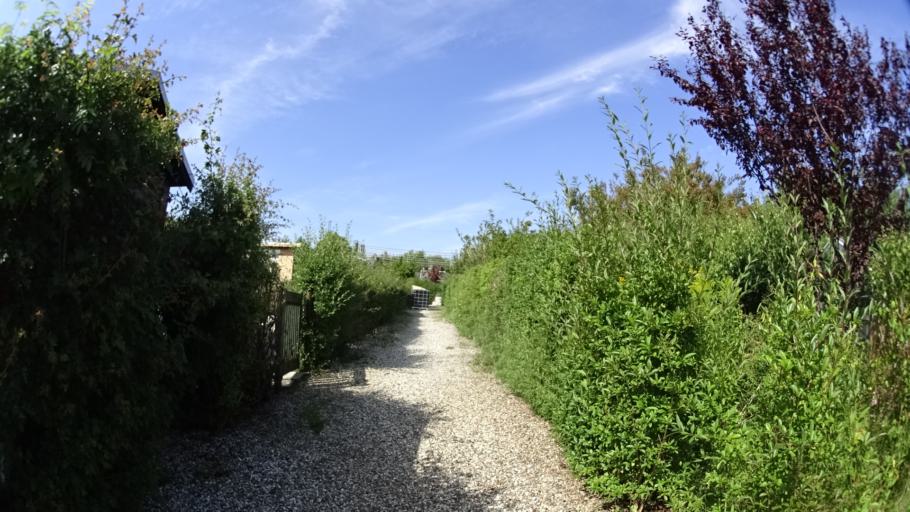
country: DK
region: Central Jutland
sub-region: Arhus Kommune
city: Stavtrup
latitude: 56.1297
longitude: 10.1472
